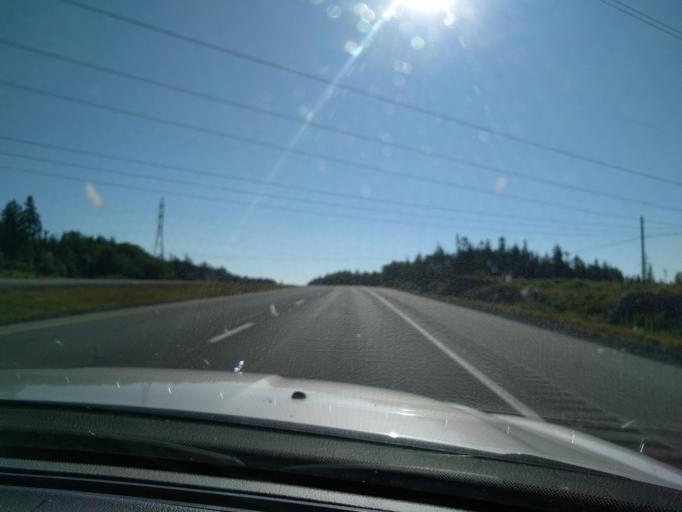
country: CA
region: New Brunswick
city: Saint John
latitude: 45.2003
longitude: -66.2423
